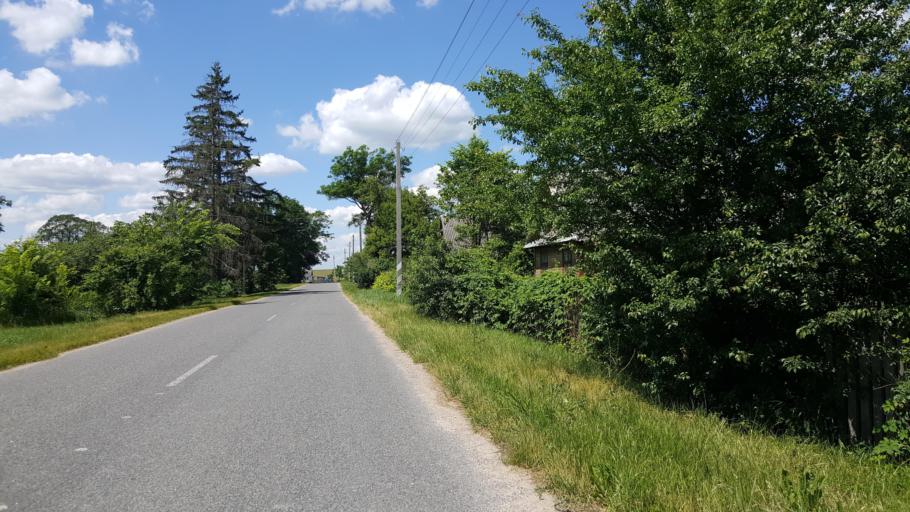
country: BY
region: Brest
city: Vysokaye
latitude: 52.4509
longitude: 23.5040
